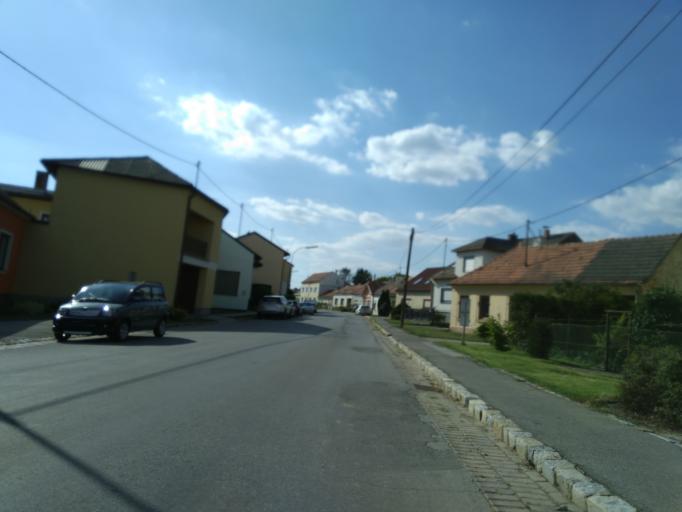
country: AT
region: Lower Austria
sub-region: Politischer Bezirk Mistelbach
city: Gross-Engersdorf
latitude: 48.3550
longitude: 16.5809
